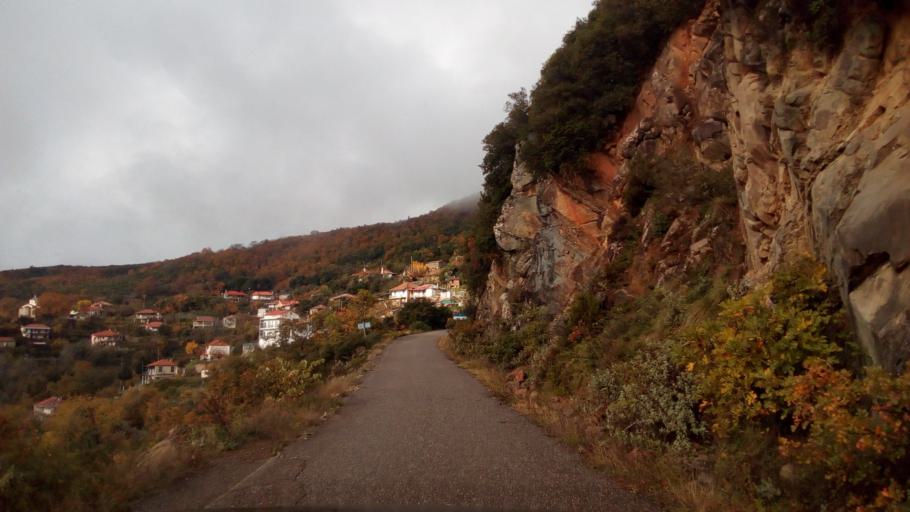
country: GR
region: West Greece
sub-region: Nomos Aitolias kai Akarnanias
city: Nafpaktos
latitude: 38.5203
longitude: 21.9682
